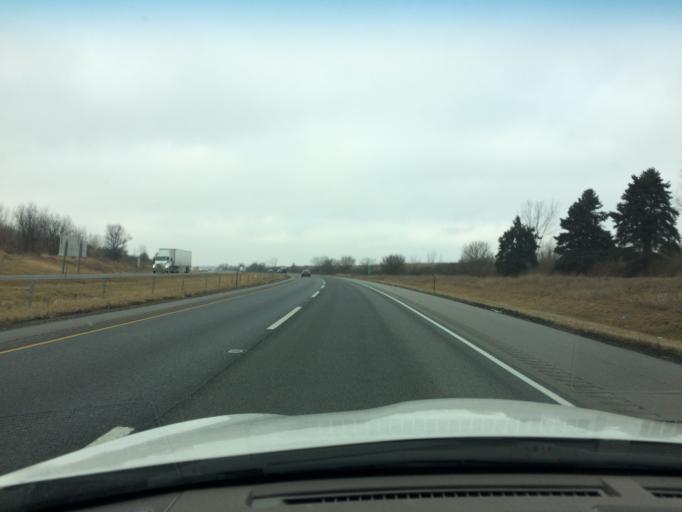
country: US
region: Illinois
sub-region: Kane County
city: Elburn
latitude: 41.8422
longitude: -88.4937
